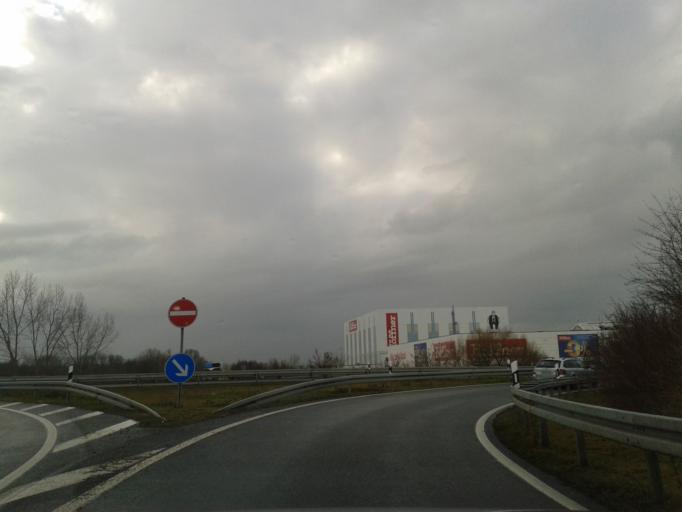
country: DE
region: Saxony-Anhalt
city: Gunthersdorf
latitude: 51.3472
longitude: 12.1844
